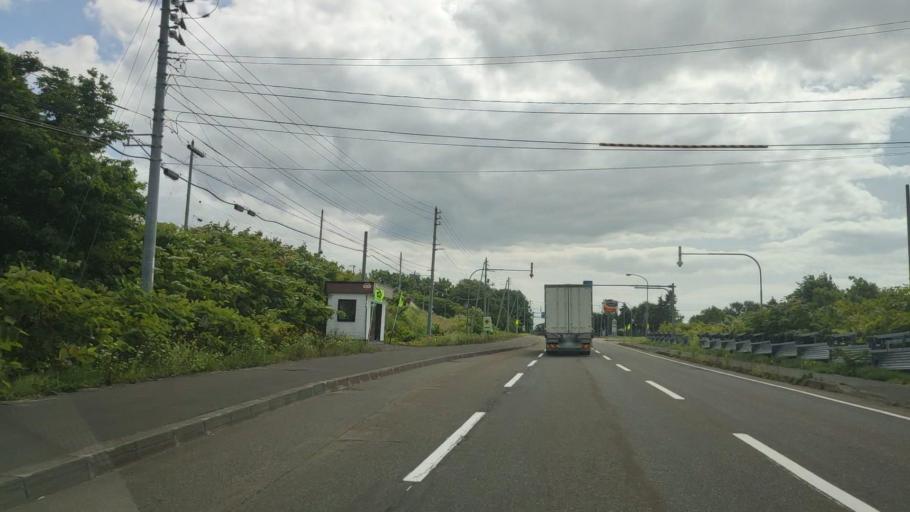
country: JP
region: Hokkaido
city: Rumoi
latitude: 44.5645
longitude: 141.7860
